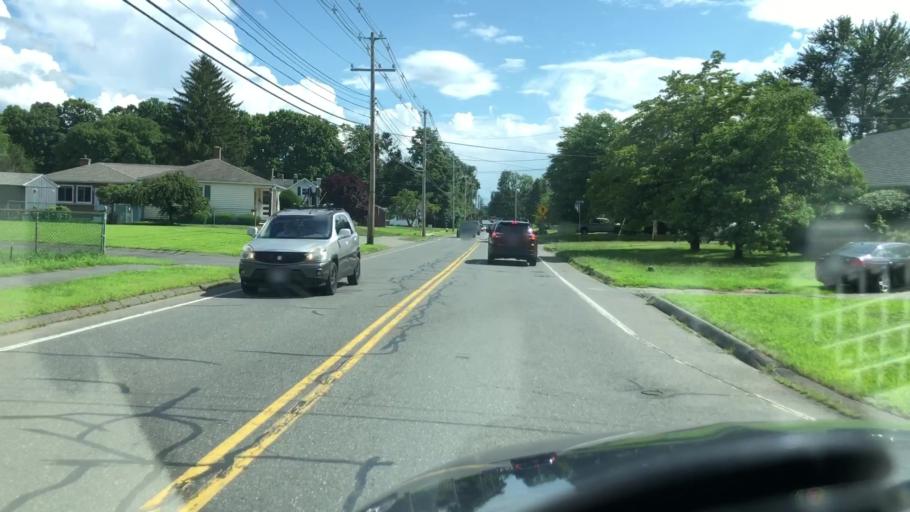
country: US
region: Massachusetts
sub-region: Hampden County
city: Holyoke
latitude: 42.1811
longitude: -72.6487
